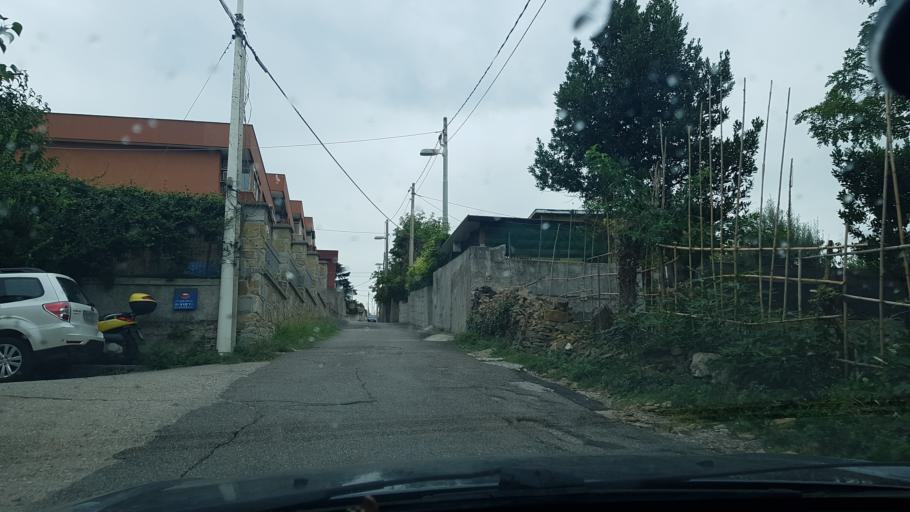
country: IT
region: Friuli Venezia Giulia
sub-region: Provincia di Trieste
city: Trieste
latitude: 45.6193
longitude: 13.7899
